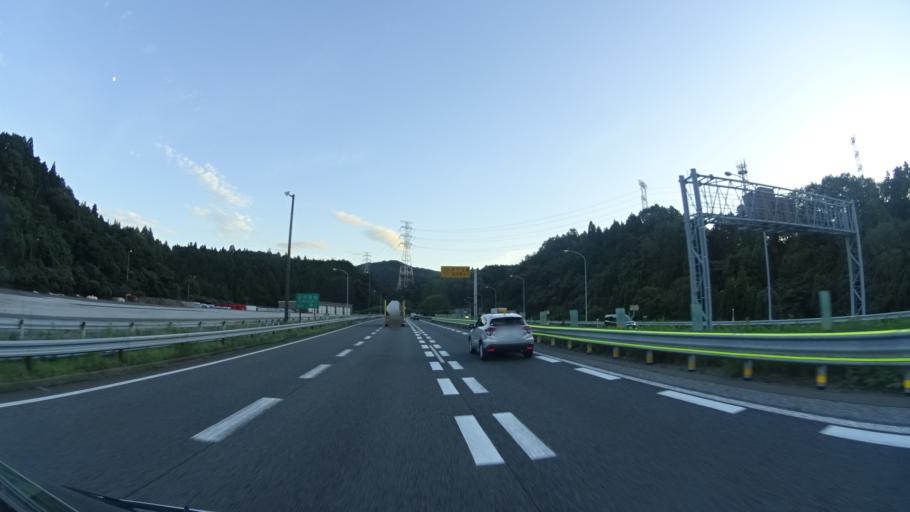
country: JP
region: Gifu
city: Tarui
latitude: 35.3521
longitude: 136.4468
